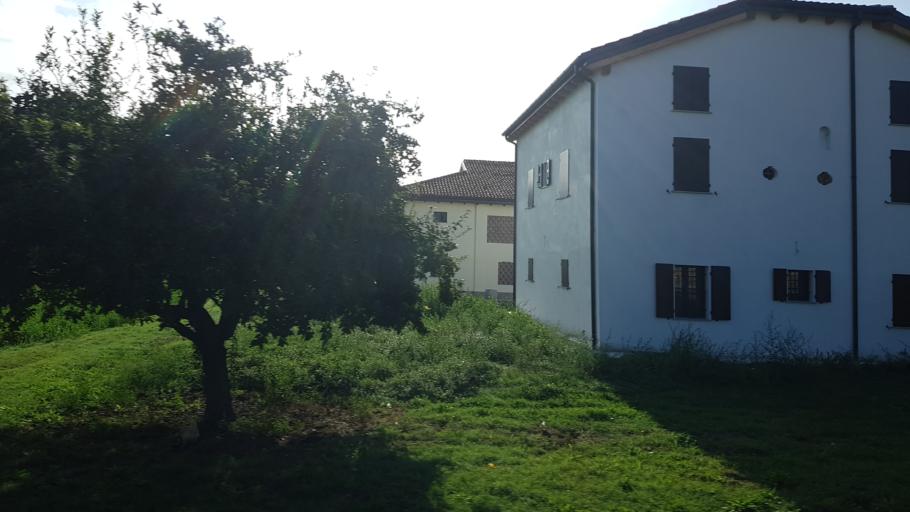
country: IT
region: Emilia-Romagna
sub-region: Provincia di Modena
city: Cavezzo
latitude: 44.8138
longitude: 11.0334
